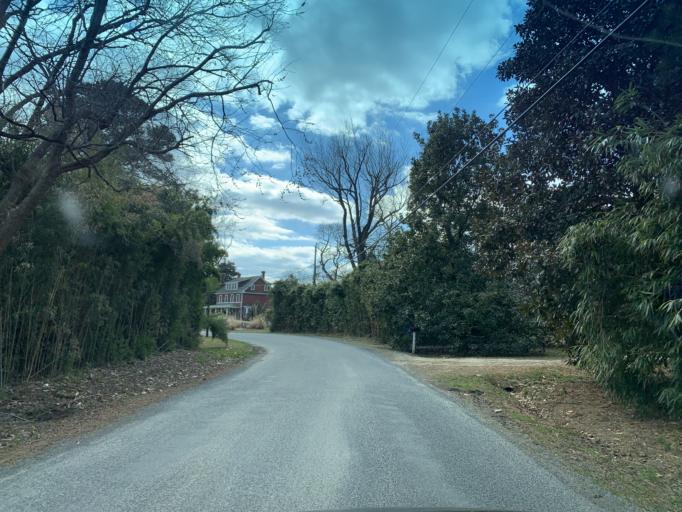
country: US
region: Maryland
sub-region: Queen Anne's County
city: Stevensville
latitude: 39.0335
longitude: -76.3107
